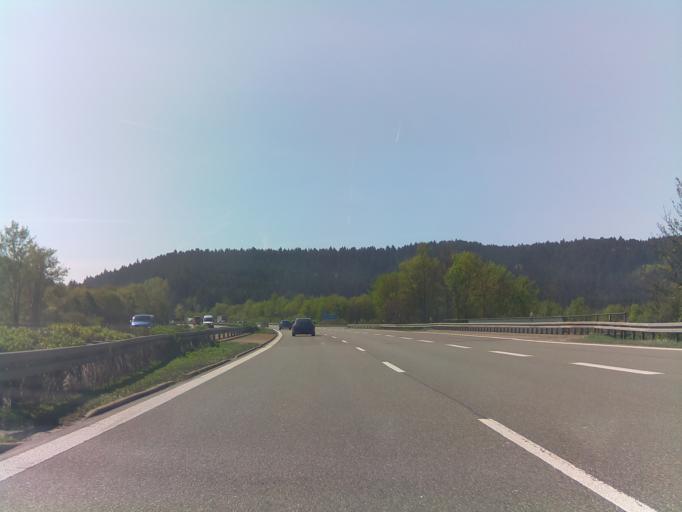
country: DE
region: Baden-Wuerttemberg
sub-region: Freiburg Region
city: Vohringen
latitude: 48.3002
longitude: 8.6348
